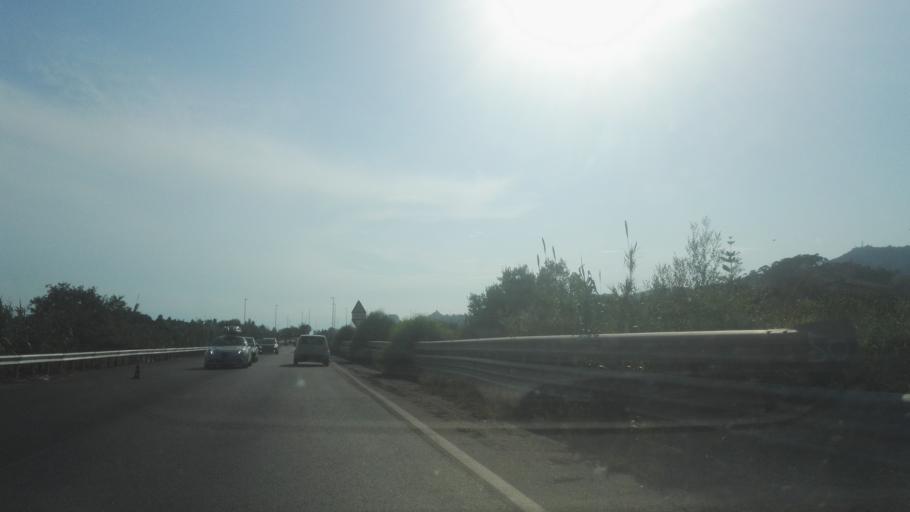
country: IT
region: Calabria
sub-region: Provincia di Reggio Calabria
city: Caulonia Marina
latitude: 38.3340
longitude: 16.4410
